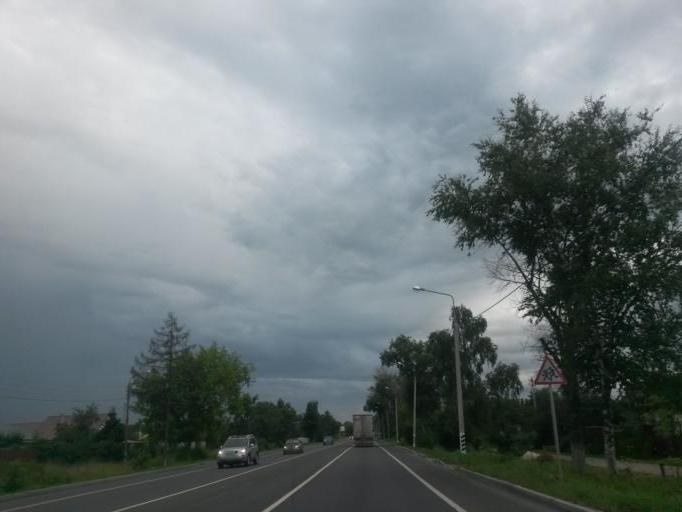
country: RU
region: Moskovskaya
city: L'vovskiy
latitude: 55.3267
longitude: 37.5284
